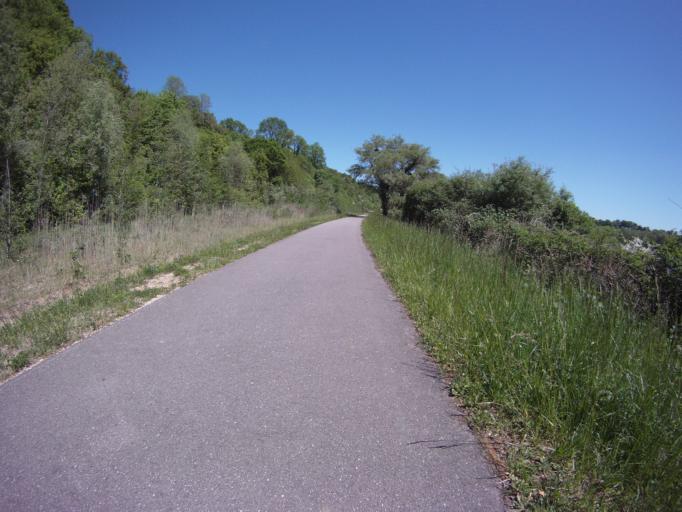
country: FR
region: Lorraine
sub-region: Departement de Meurthe-et-Moselle
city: Villey-Saint-Etienne
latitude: 48.7355
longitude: 5.9847
